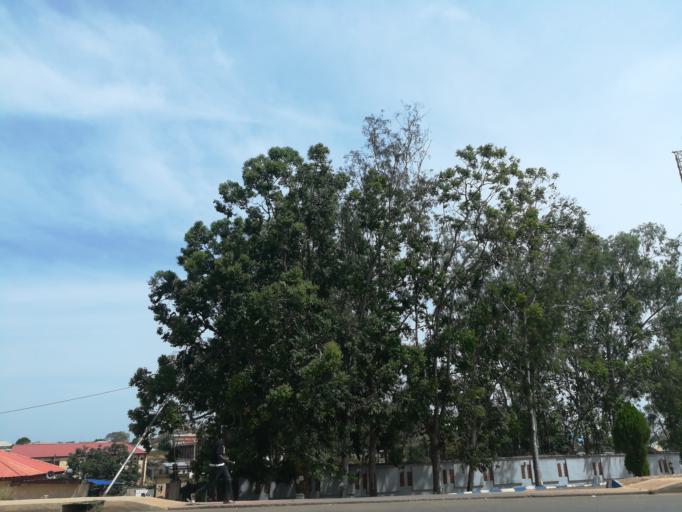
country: NG
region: Plateau
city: Bukuru
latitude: 9.8440
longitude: 8.8663
